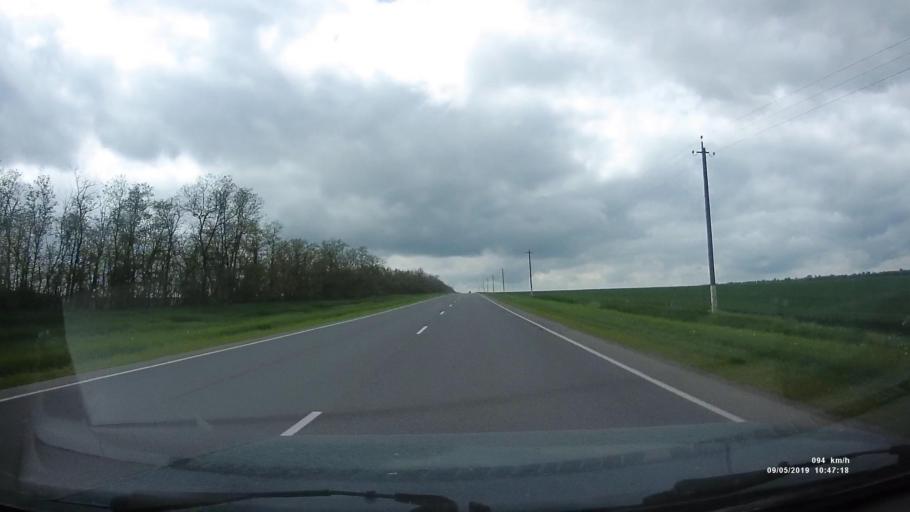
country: RU
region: Rostov
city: Peshkovo
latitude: 46.9725
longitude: 39.3556
